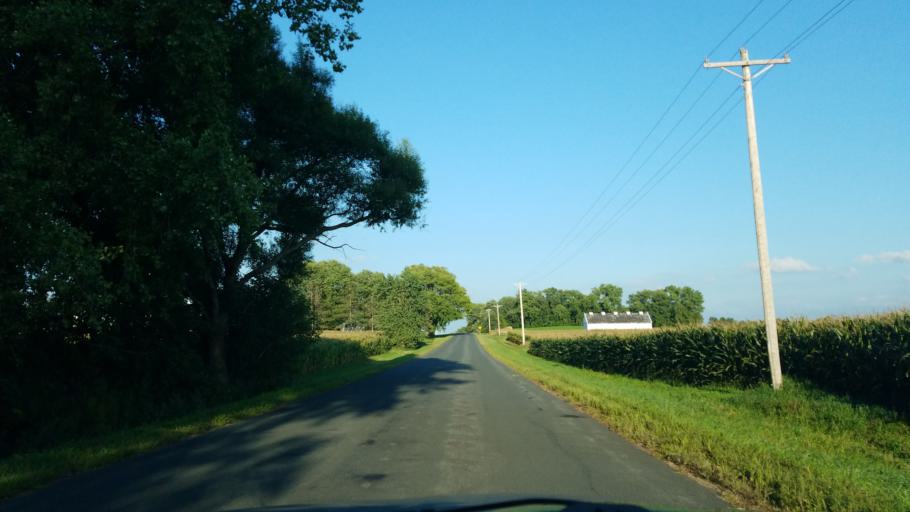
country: US
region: Wisconsin
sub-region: Saint Croix County
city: Roberts
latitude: 45.0071
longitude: -92.5452
